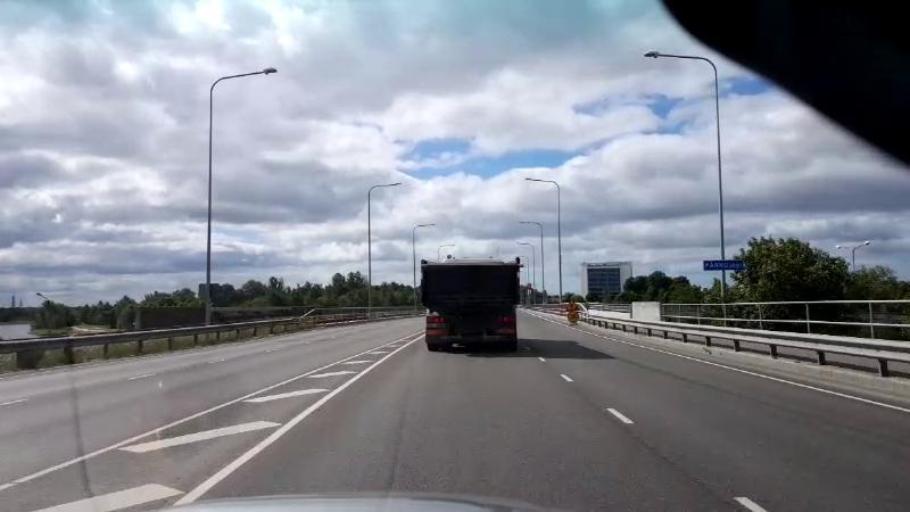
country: EE
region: Paernumaa
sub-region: Paernu linn
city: Parnu
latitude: 58.3776
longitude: 24.5553
